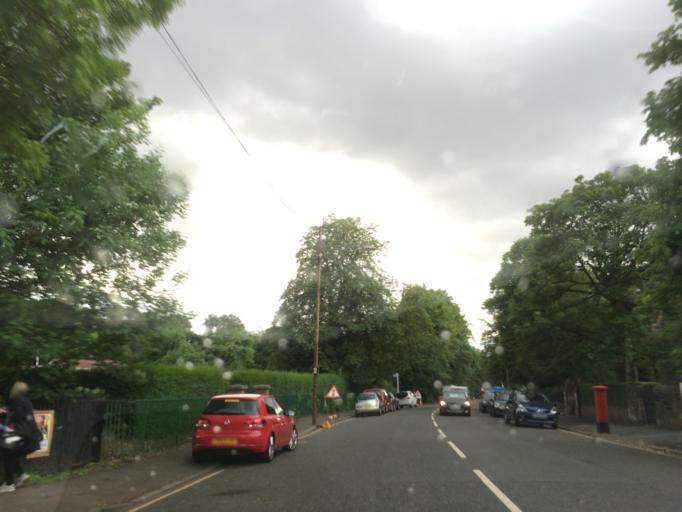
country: GB
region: Scotland
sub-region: Glasgow City
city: Glasgow
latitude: 55.8315
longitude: -4.2609
